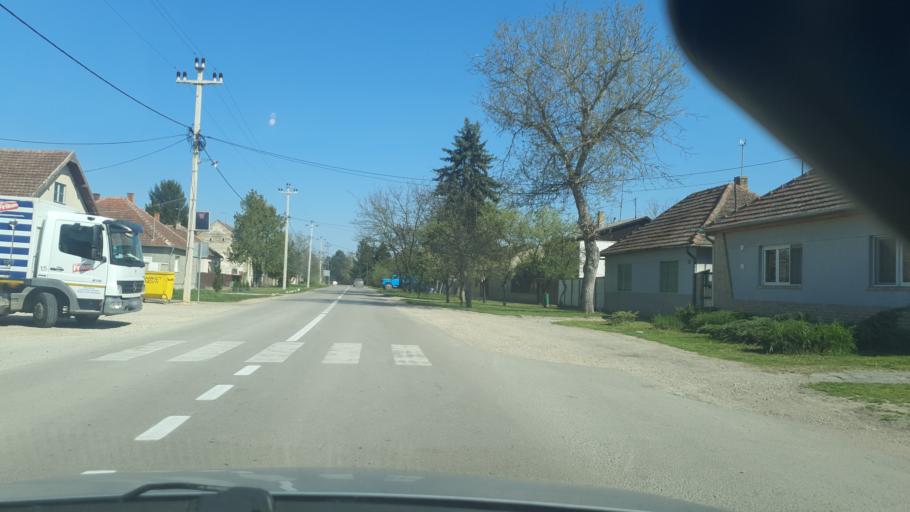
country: RS
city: Kolut
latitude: 45.8542
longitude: 18.9327
